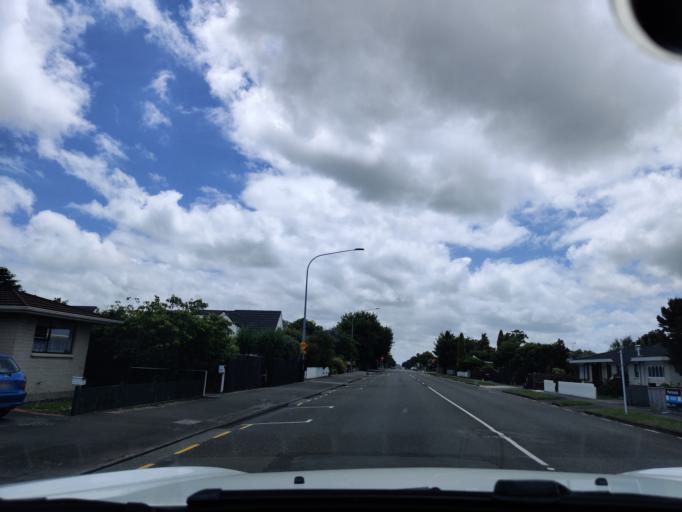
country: NZ
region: Manawatu-Wanganui
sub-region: Palmerston North City
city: Palmerston North
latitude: -40.3618
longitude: 175.6330
